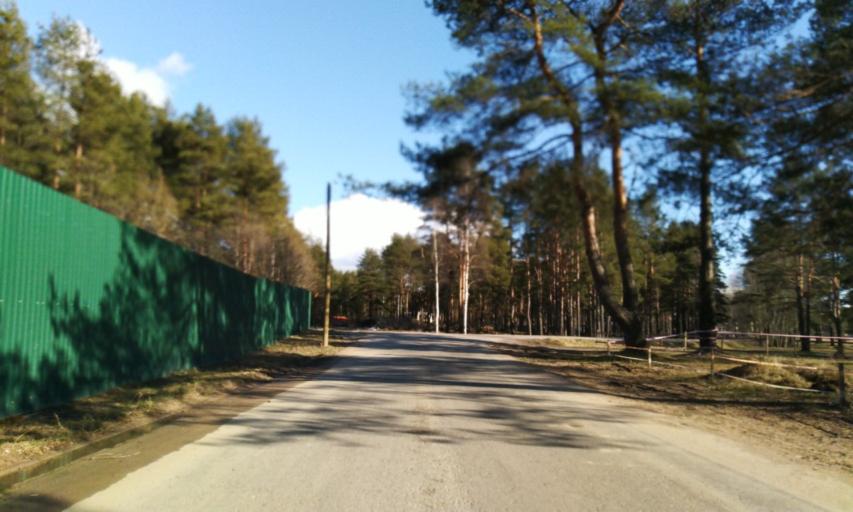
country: RU
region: Leningrad
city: Novoye Devyatkino
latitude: 60.1208
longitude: 30.4461
